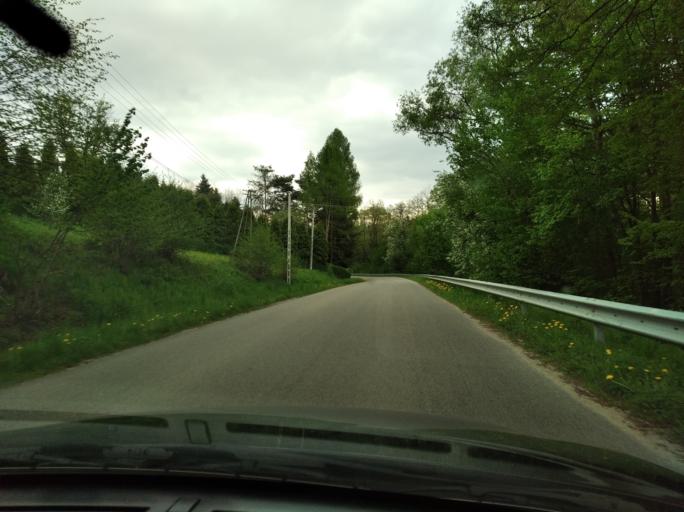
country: PL
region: Subcarpathian Voivodeship
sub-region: Powiat debicki
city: Leki Gorne
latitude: 49.9777
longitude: 21.1601
